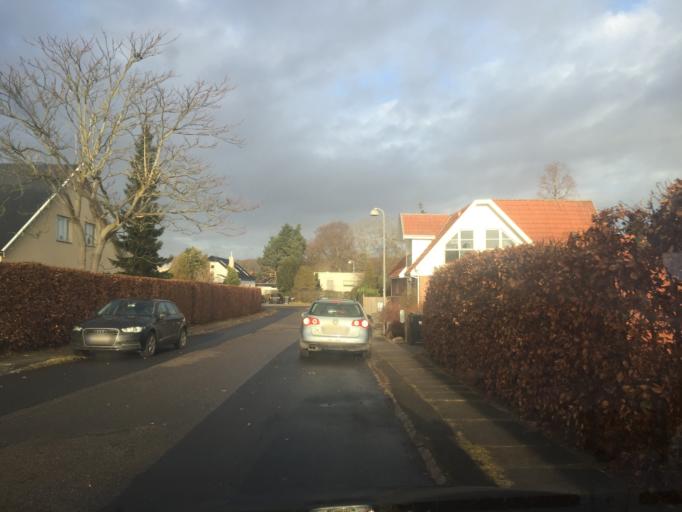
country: DK
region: Capital Region
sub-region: Fureso Kommune
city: Vaerlose
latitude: 55.7570
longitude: 12.4054
